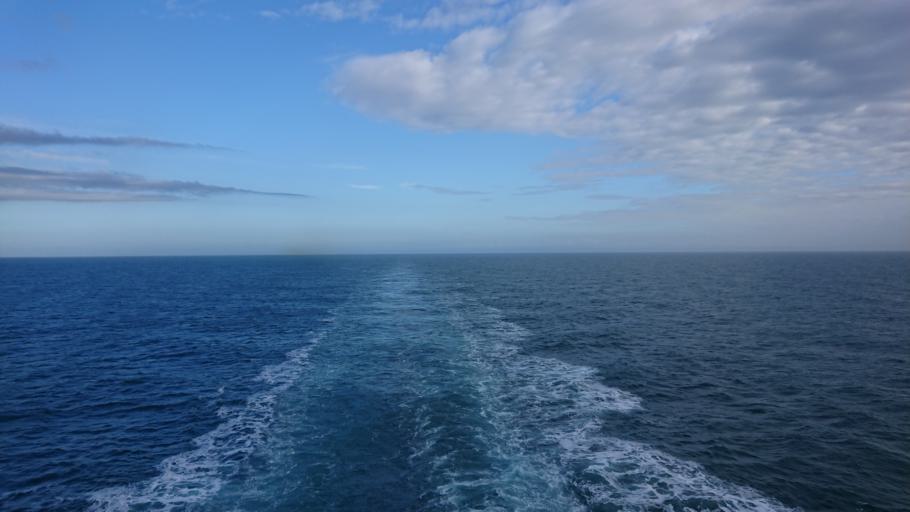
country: GB
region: Wales
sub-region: Pembrokeshire
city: Saint David's
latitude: 52.1357
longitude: -5.6226
